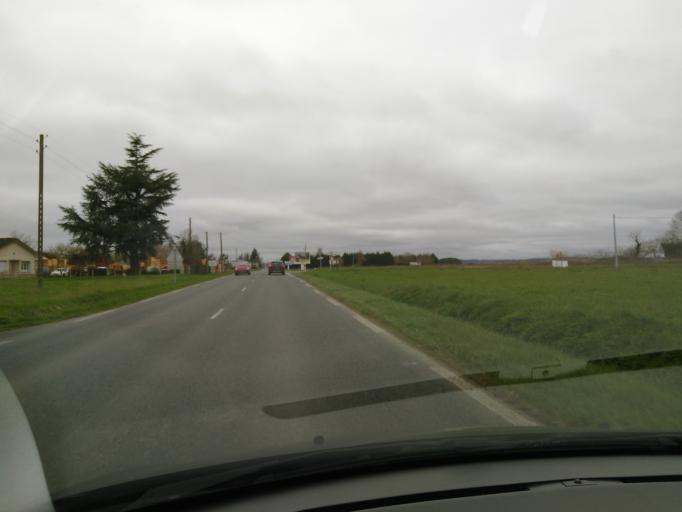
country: FR
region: Aquitaine
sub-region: Departement de la Dordogne
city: Monbazillac
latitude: 44.8178
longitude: 0.5051
